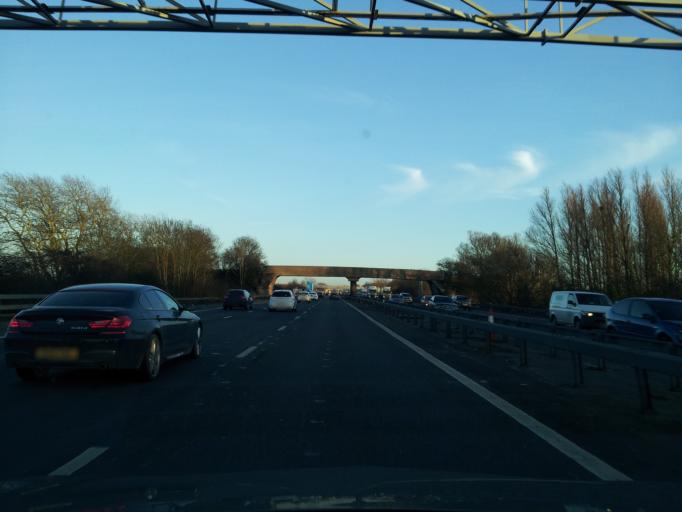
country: GB
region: England
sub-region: Central Bedfordshire
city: Husborne Crawley
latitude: 52.0300
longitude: -0.6171
